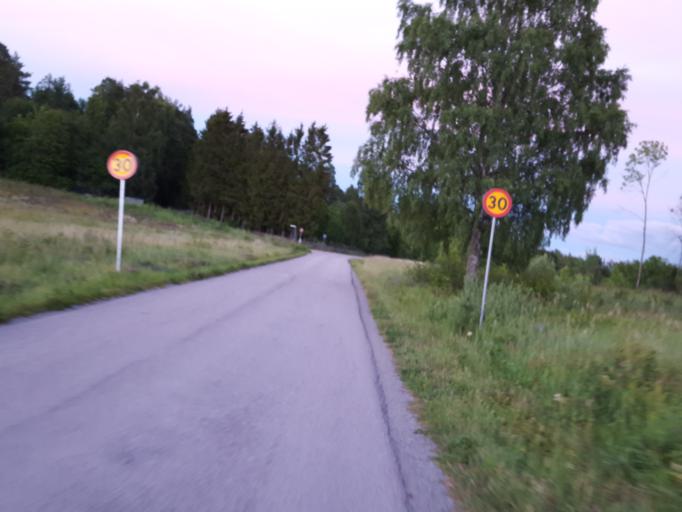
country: SE
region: Uppsala
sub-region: Uppsala Kommun
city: Uppsala
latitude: 59.7822
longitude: 17.5986
